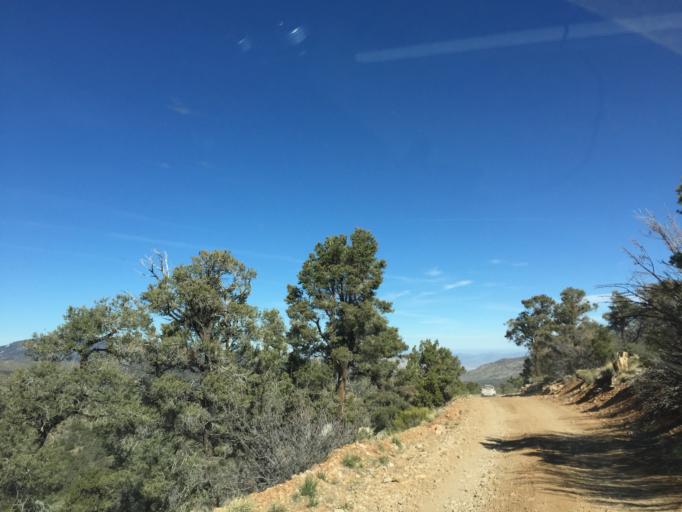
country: US
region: California
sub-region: San Bernardino County
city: Big Bear City
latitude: 34.2425
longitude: -116.7210
